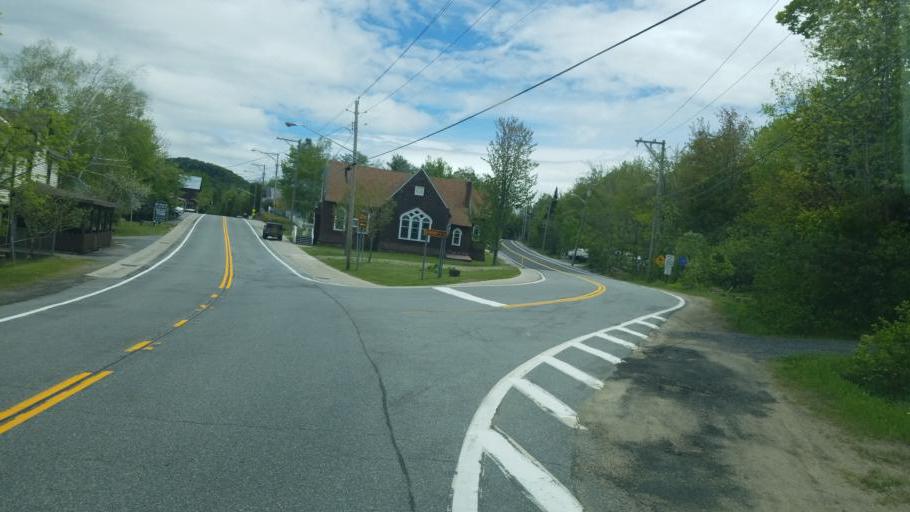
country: US
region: New York
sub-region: Franklin County
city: Tupper Lake
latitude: 43.8544
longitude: -74.4388
